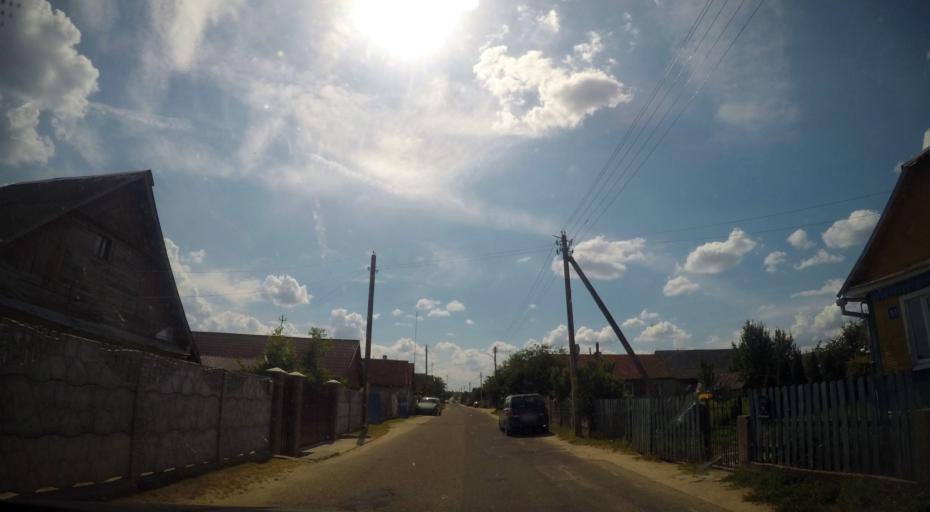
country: BY
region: Grodnenskaya
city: Hrodna
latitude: 53.6276
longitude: 23.8405
